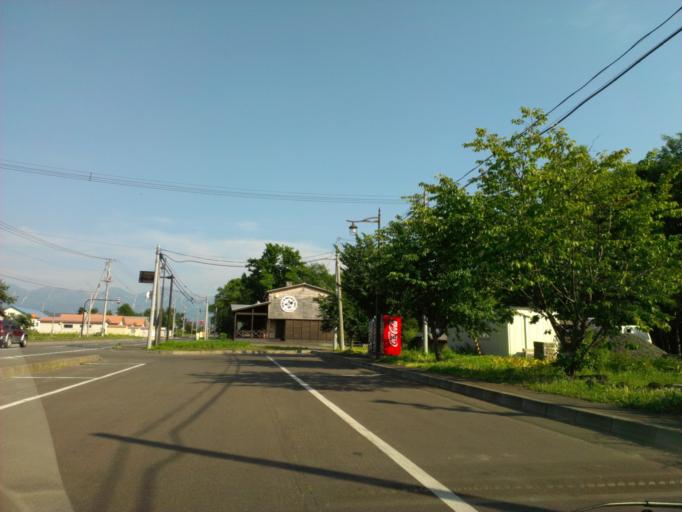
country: JP
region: Hokkaido
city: Shimo-furano
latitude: 43.5458
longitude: 142.5298
